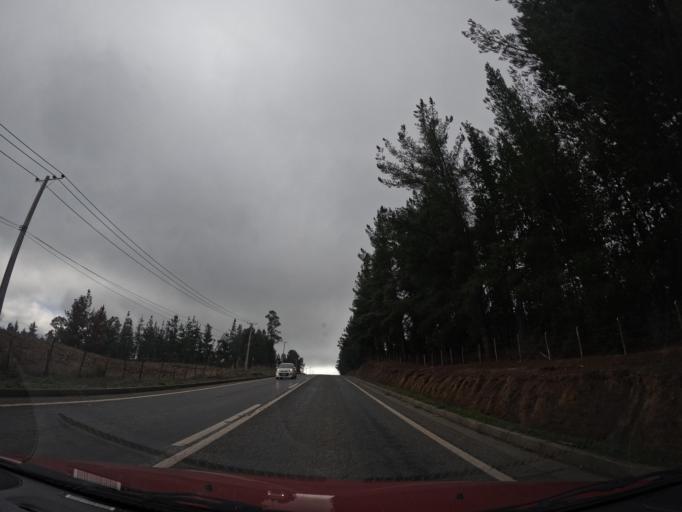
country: CL
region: Maule
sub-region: Provincia de Cauquenes
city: Cauquenes
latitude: -36.2494
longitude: -72.5483
